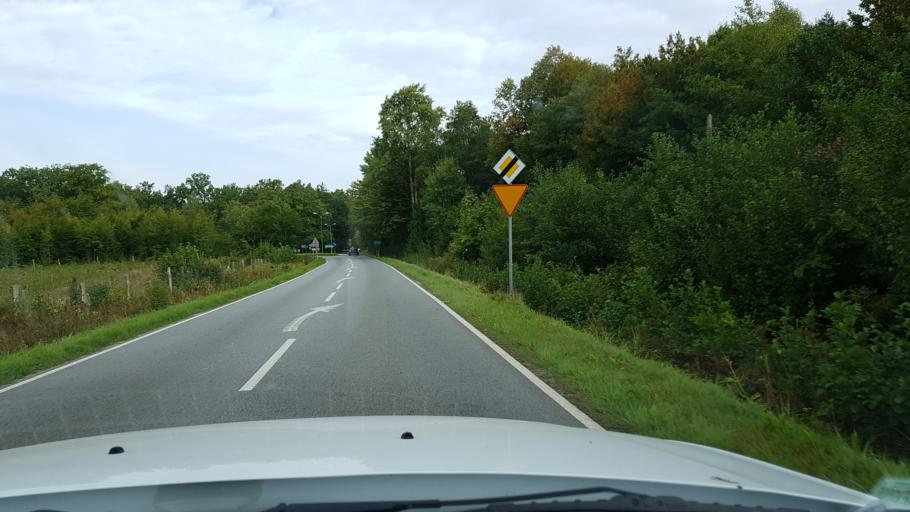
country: PL
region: West Pomeranian Voivodeship
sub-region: Powiat slawienski
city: Slawno
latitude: 54.3856
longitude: 16.6165
